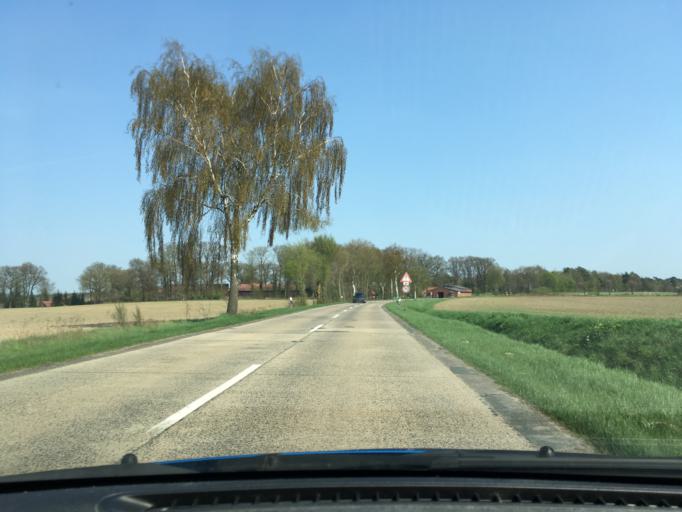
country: DE
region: Lower Saxony
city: Sudergellersen
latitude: 53.1927
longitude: 10.3183
